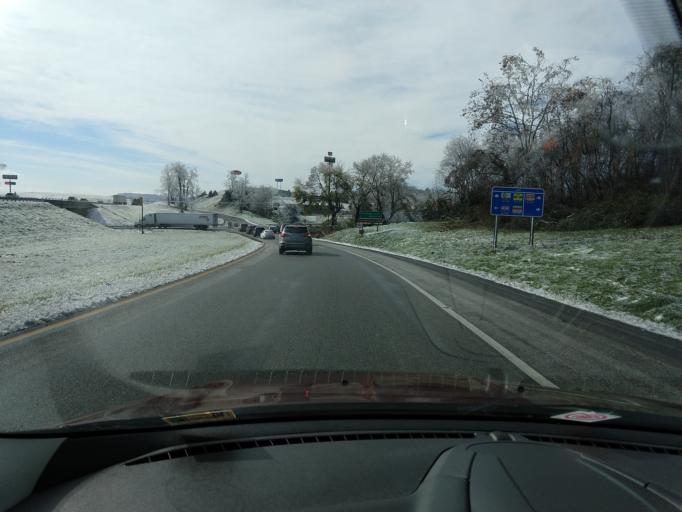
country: US
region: Virginia
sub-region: Augusta County
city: Stuarts Draft
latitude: 37.9340
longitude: -79.2275
